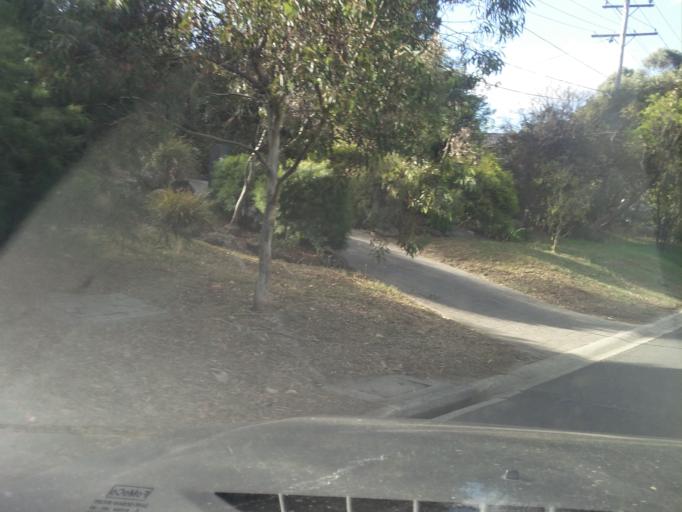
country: AU
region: Victoria
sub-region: Nillumbik
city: Eltham
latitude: -37.7220
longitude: 145.1605
